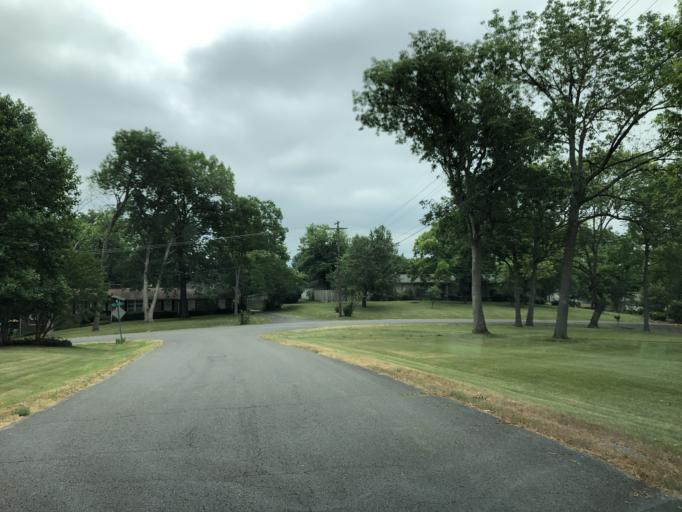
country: US
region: Tennessee
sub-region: Davidson County
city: Goodlettsville
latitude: 36.2822
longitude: -86.7341
